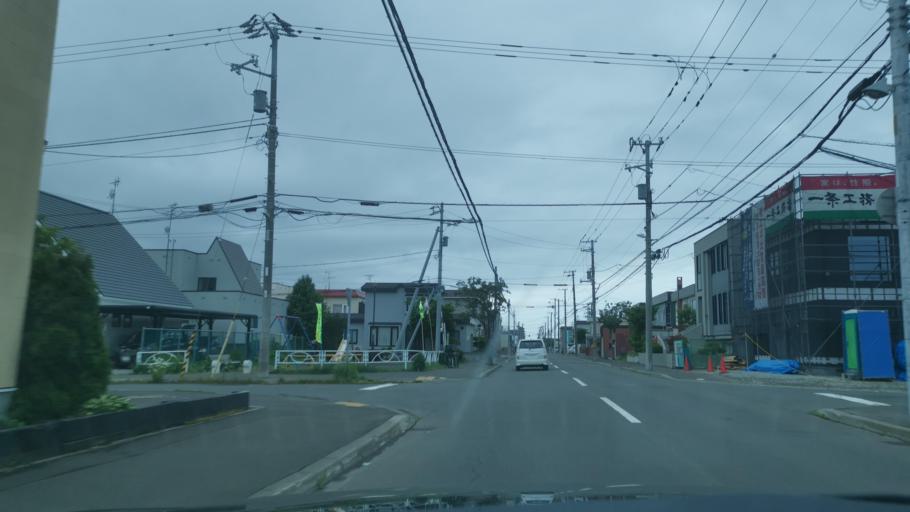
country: JP
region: Hokkaido
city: Sapporo
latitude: 43.1065
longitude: 141.3046
